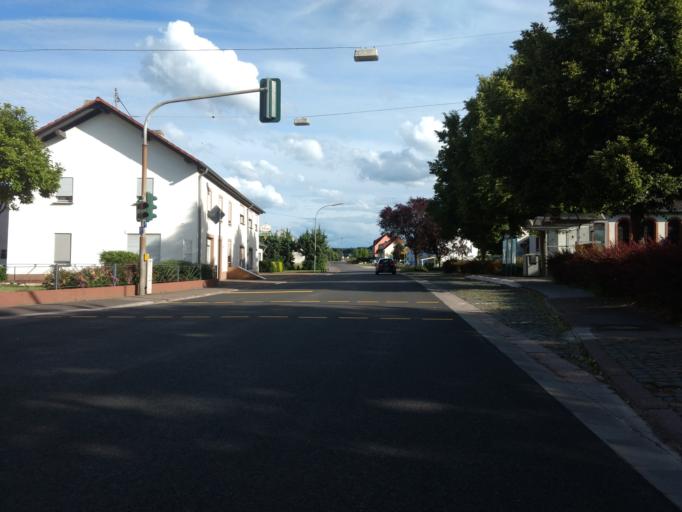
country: DE
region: Saarland
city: Merzig
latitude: 49.4505
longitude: 6.6035
